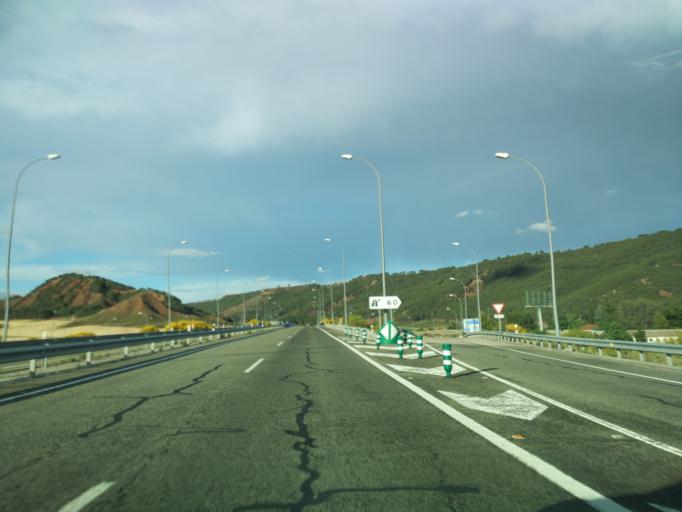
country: ES
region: Castille-La Mancha
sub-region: Provincia de Guadalajara
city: Tortola de Henares
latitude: 40.6608
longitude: -3.1221
